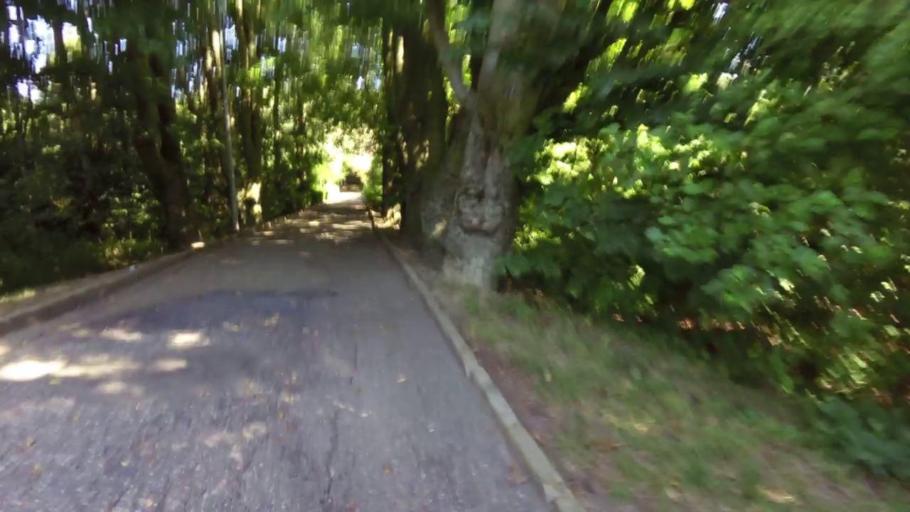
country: PL
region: West Pomeranian Voivodeship
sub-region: Powiat drawski
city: Zlocieniec
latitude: 53.5361
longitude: 16.0075
